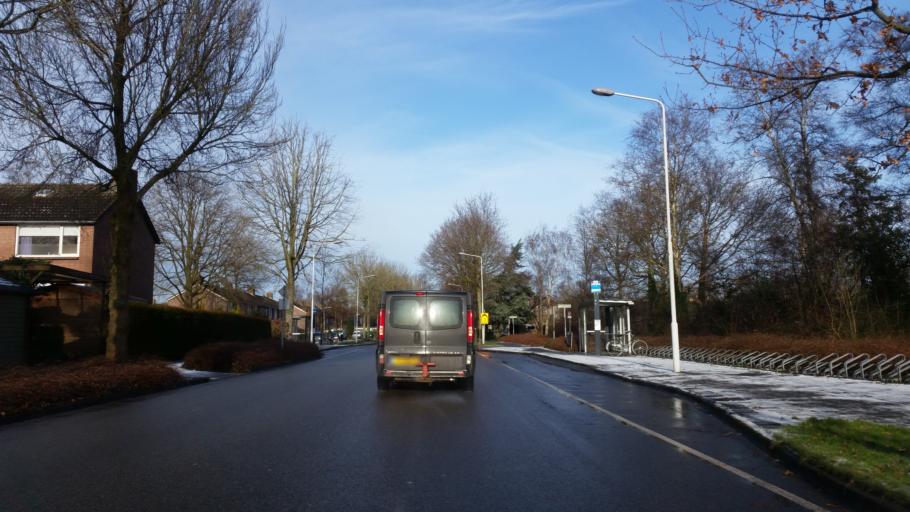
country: NL
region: Friesland
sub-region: Gemeente Tytsjerksteradiel
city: Sumar
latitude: 53.1896
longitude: 5.9985
